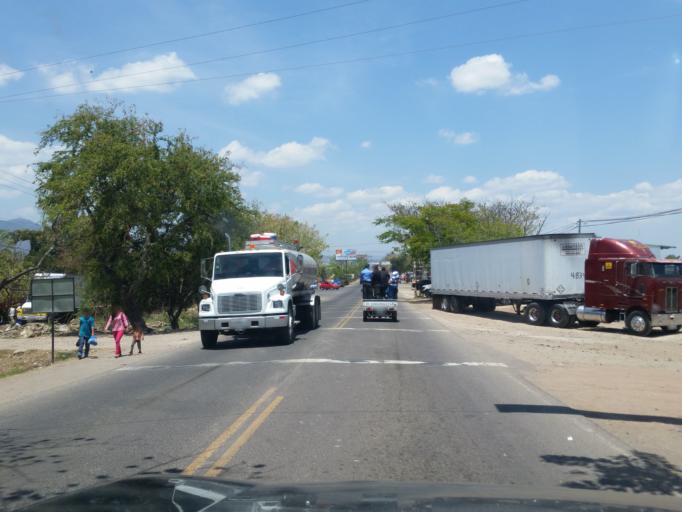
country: NI
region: Esteli
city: Esteli
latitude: 13.0649
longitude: -86.3474
